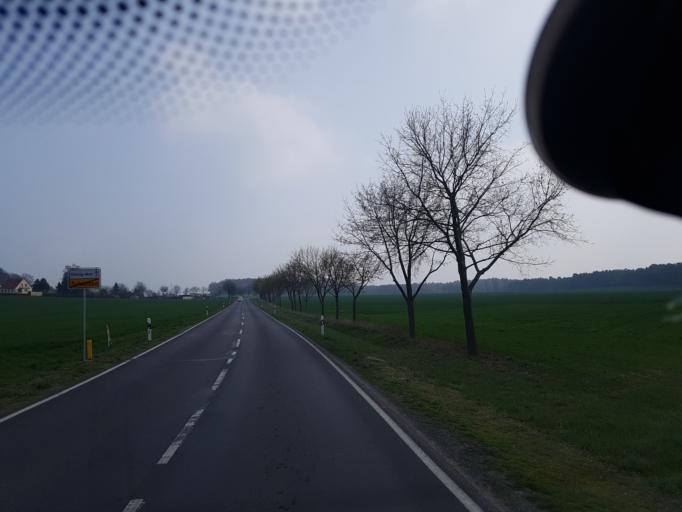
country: DE
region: Brandenburg
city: Schlieben
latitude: 51.7203
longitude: 13.3798
